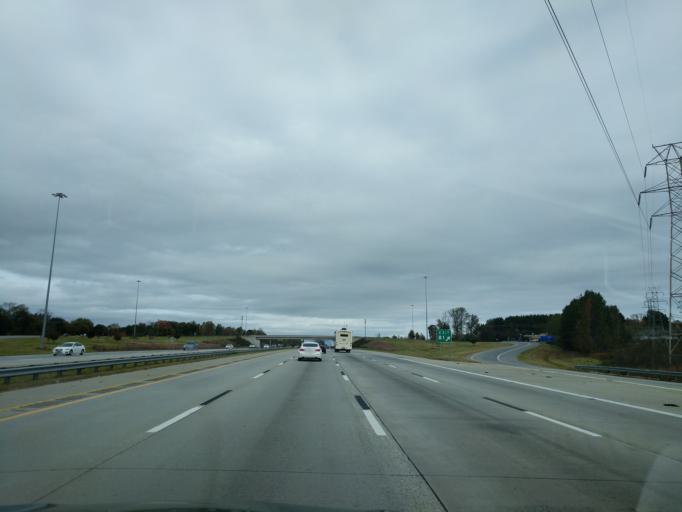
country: US
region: North Carolina
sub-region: Rowan County
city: East Spencer
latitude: 35.6912
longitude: -80.4024
